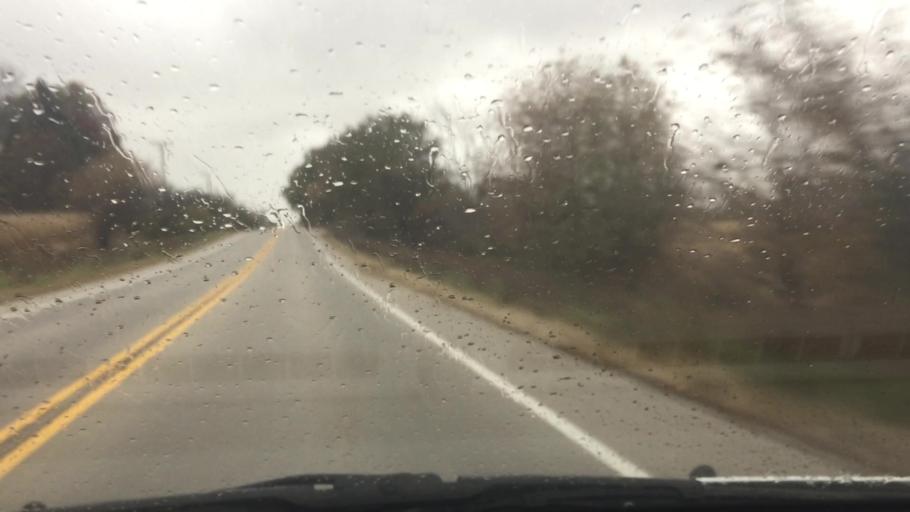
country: US
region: Illinois
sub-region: McHenry County
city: McCullom Lake
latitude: 42.4103
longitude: -88.3011
